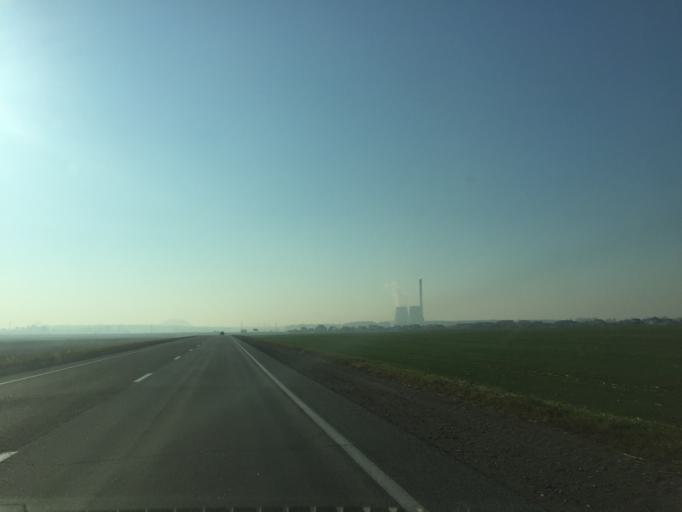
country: BY
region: Gomel
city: Kastsyukowka
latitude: 52.4709
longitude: 30.8232
